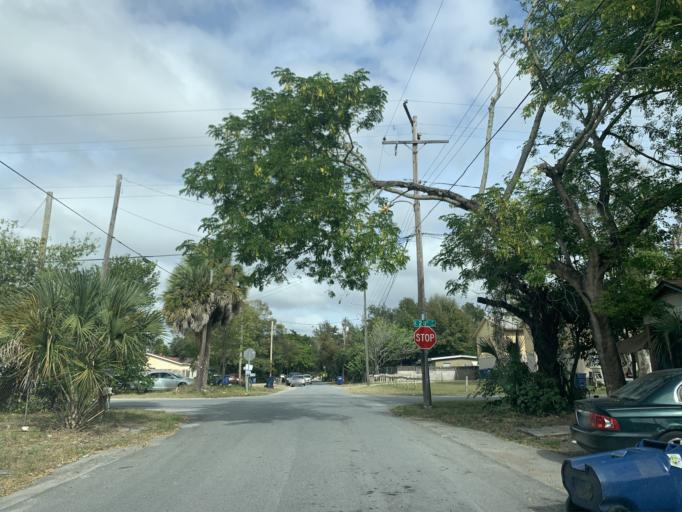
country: US
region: Florida
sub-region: Hillsborough County
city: East Lake-Orient Park
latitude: 27.9758
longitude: -82.3993
